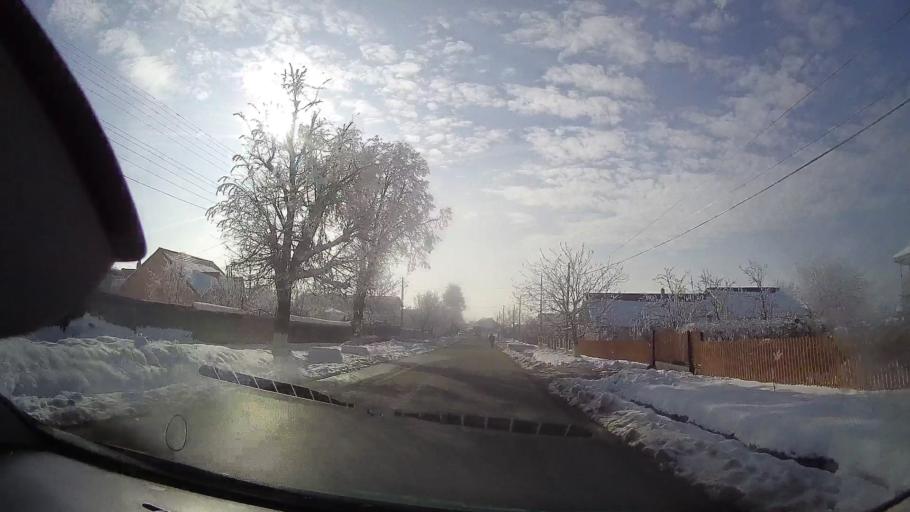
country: RO
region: Iasi
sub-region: Comuna Cristesti
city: Cristesti
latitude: 47.2523
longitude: 26.5692
